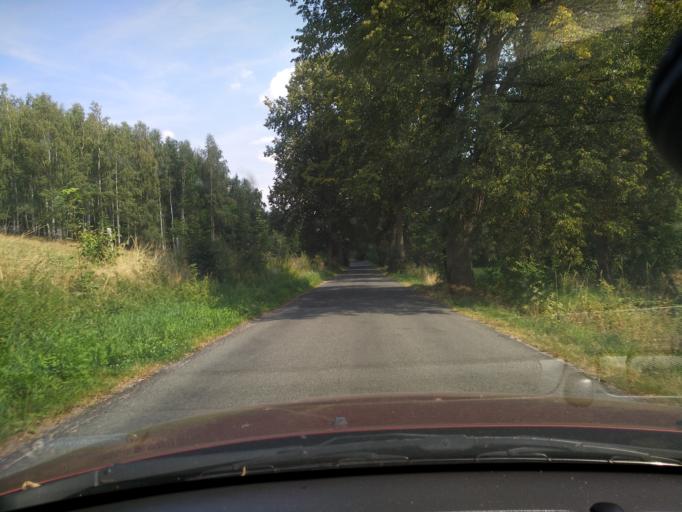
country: PL
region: Lower Silesian Voivodeship
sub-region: Powiat jeleniogorski
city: Stara Kamienica
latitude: 50.8968
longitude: 15.5634
